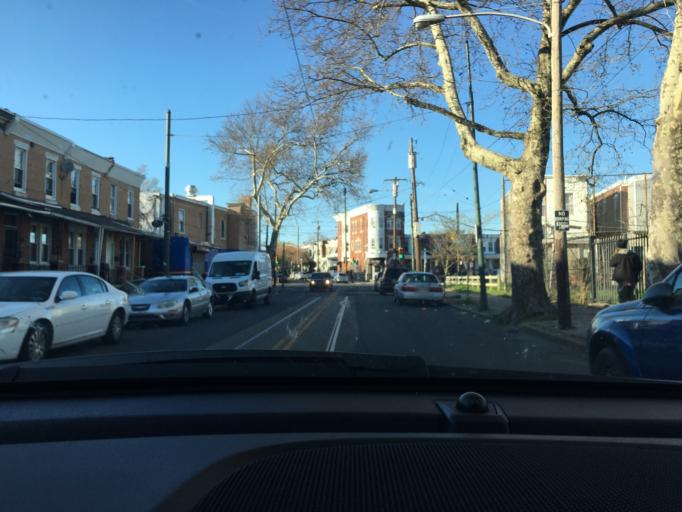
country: US
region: Pennsylvania
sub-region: Delaware County
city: Millbourne
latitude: 39.9678
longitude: -75.2355
